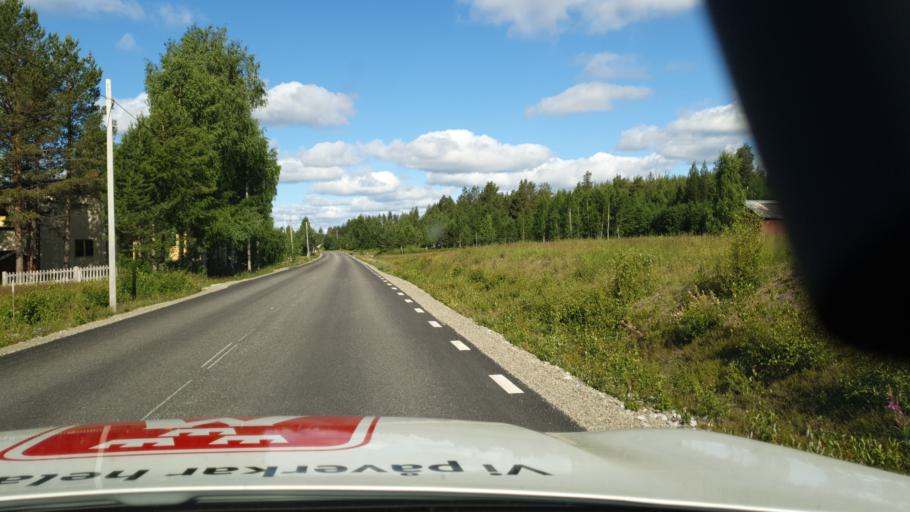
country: SE
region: Vaesterbotten
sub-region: Lycksele Kommun
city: Lycksele
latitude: 64.7598
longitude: 19.0671
